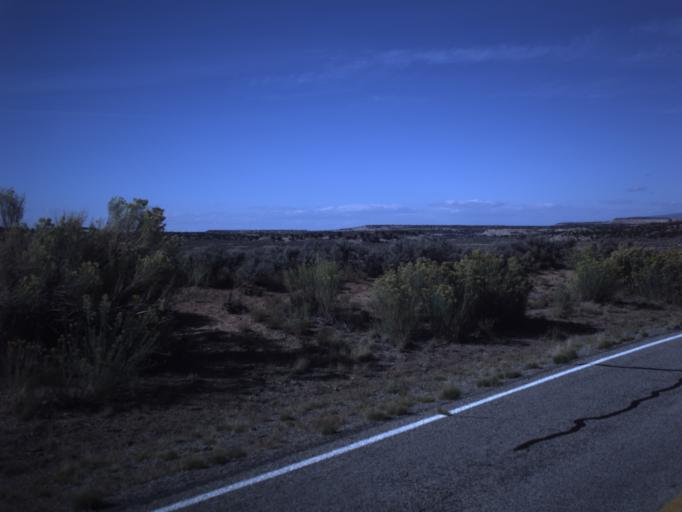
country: US
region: Utah
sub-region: San Juan County
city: Monticello
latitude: 38.0159
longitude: -109.4314
